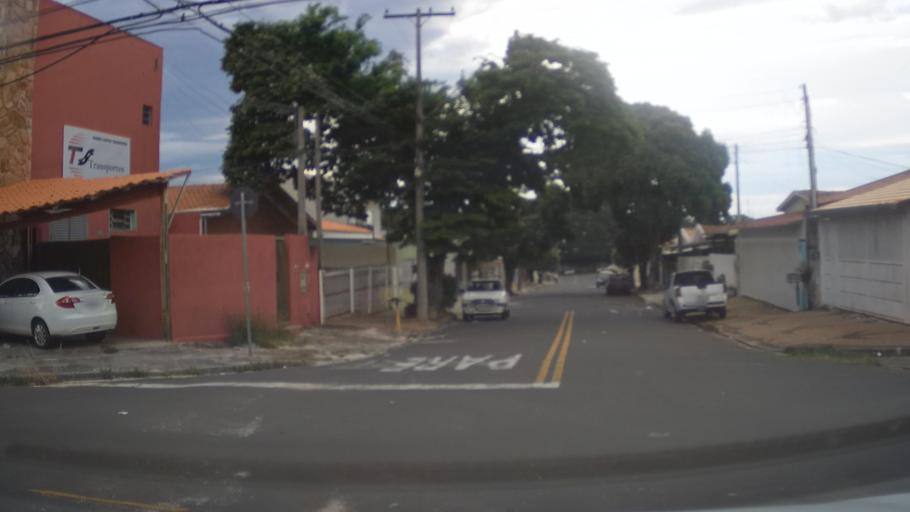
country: BR
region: Sao Paulo
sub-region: Campinas
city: Campinas
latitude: -22.8916
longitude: -47.1090
